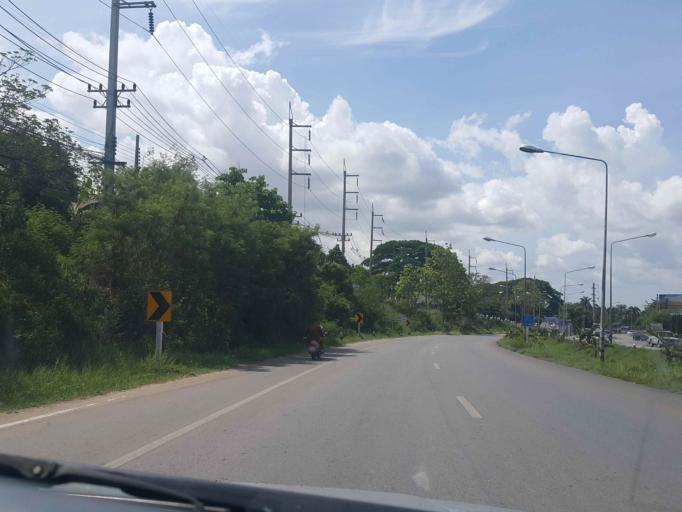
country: TH
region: Phayao
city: Phayao
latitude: 19.1628
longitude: 99.9134
